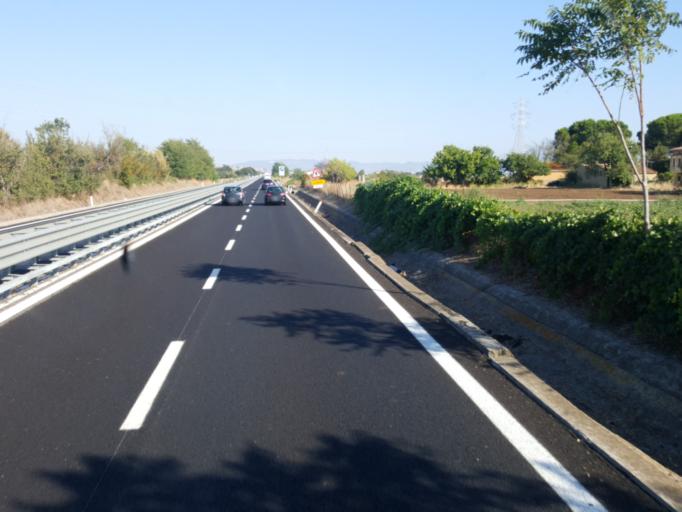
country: IT
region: Latium
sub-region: Provincia di Viterbo
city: Tarquinia
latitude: 42.2812
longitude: 11.6950
